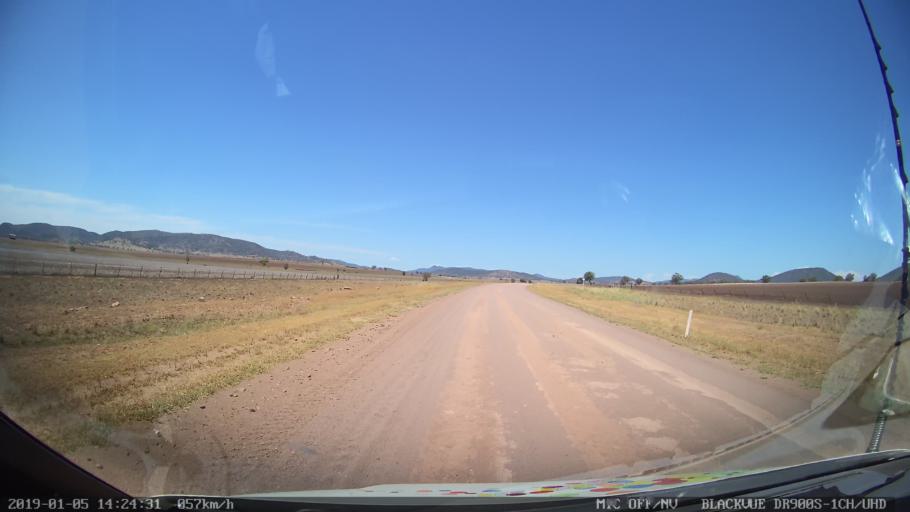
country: AU
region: New South Wales
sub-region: Liverpool Plains
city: Quirindi
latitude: -31.2418
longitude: 150.5403
